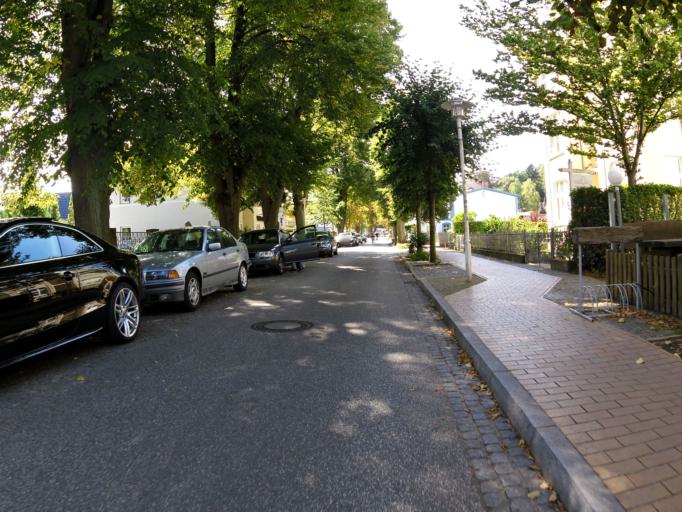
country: DE
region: Mecklenburg-Vorpommern
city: Seebad Bansin
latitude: 53.9700
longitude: 14.1408
